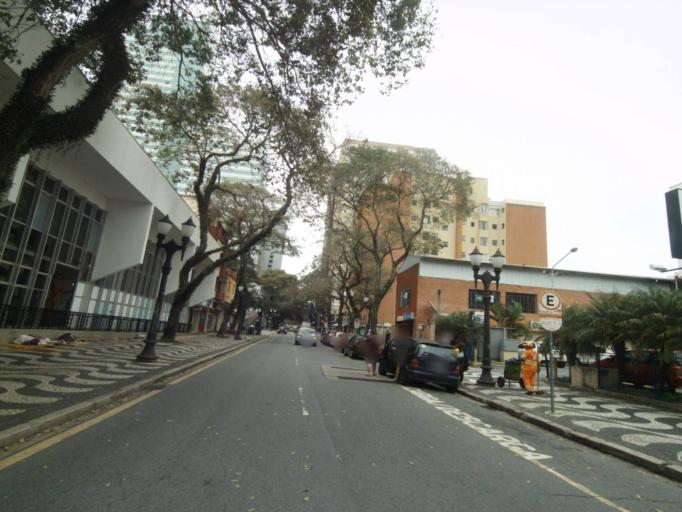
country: BR
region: Parana
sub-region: Curitiba
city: Curitiba
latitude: -25.4360
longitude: -49.2792
